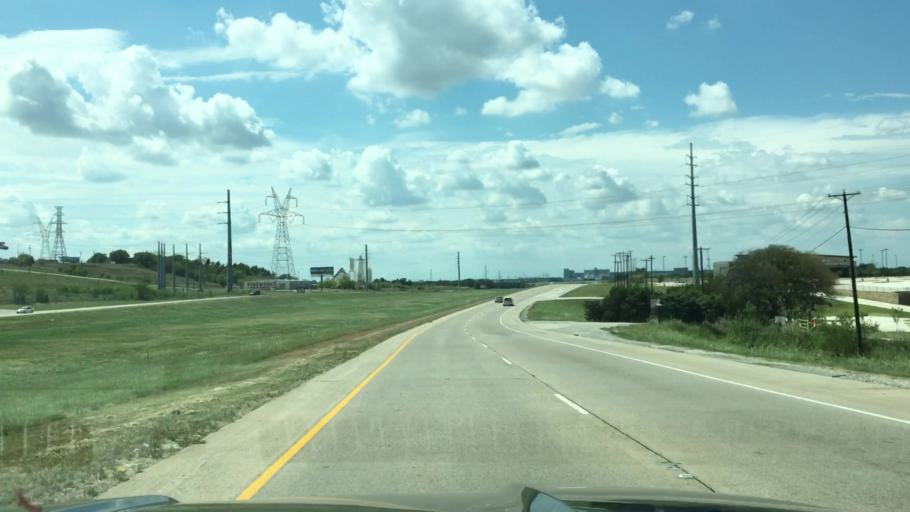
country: US
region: Texas
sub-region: Denton County
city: Roanoke
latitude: 33.0165
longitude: -97.2360
